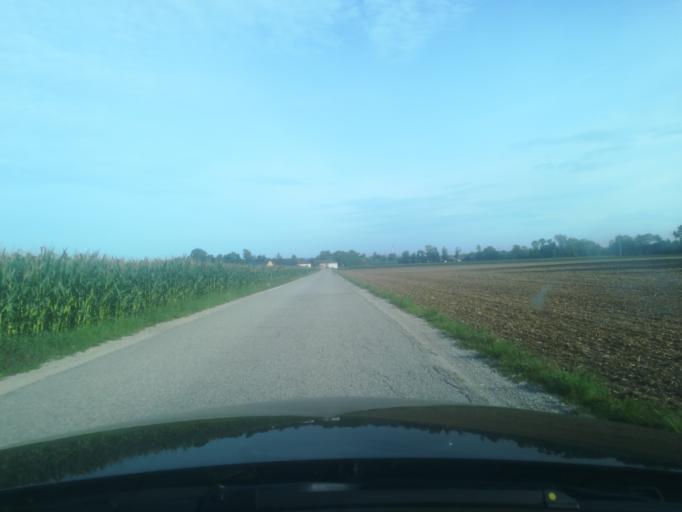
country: AT
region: Upper Austria
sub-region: Wels-Land
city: Marchtrenk
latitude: 48.1757
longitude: 14.1602
